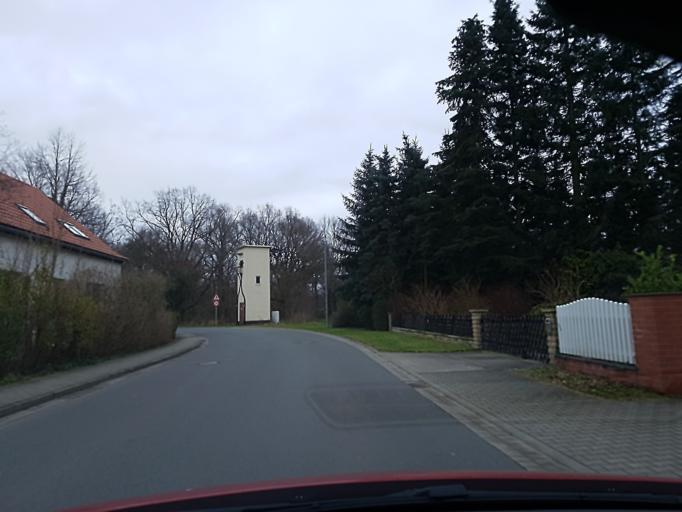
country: DE
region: Brandenburg
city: Elsterwerda
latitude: 51.4480
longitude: 13.5143
